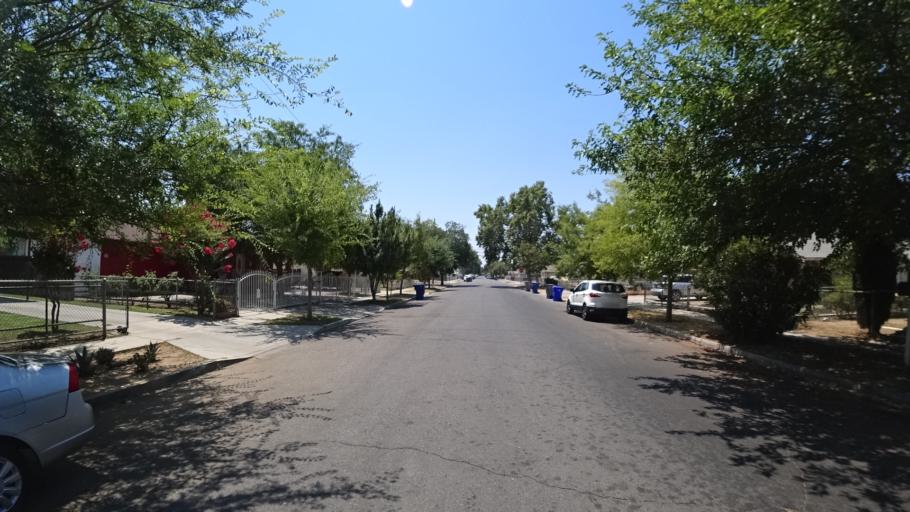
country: US
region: California
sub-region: Fresno County
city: Fresno
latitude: 36.7184
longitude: -119.7942
